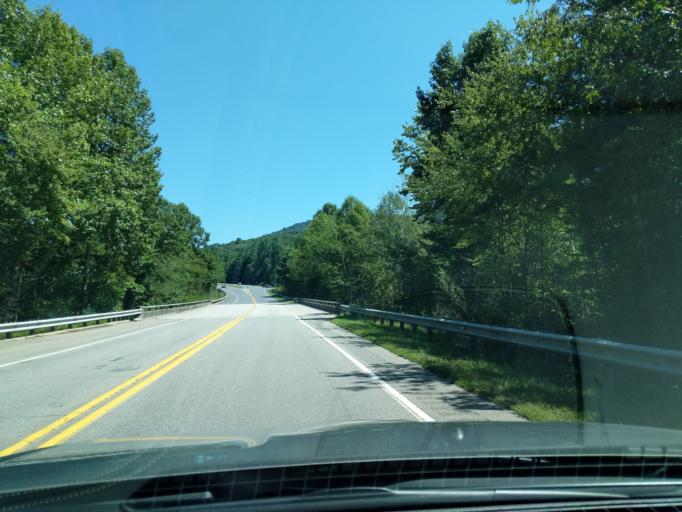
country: US
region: North Carolina
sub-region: Macon County
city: Franklin
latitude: 35.1378
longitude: -83.4894
